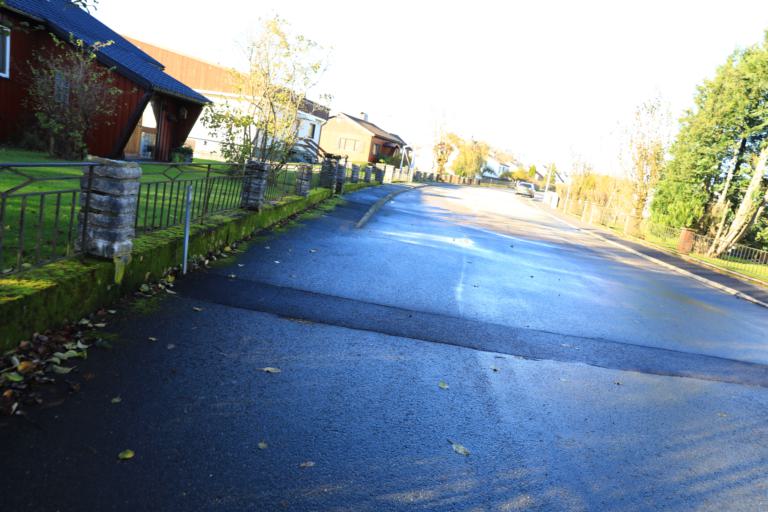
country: SE
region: Vaestra Goetaland
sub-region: Marks Kommun
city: Kinna
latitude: 57.4992
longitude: 12.6769
